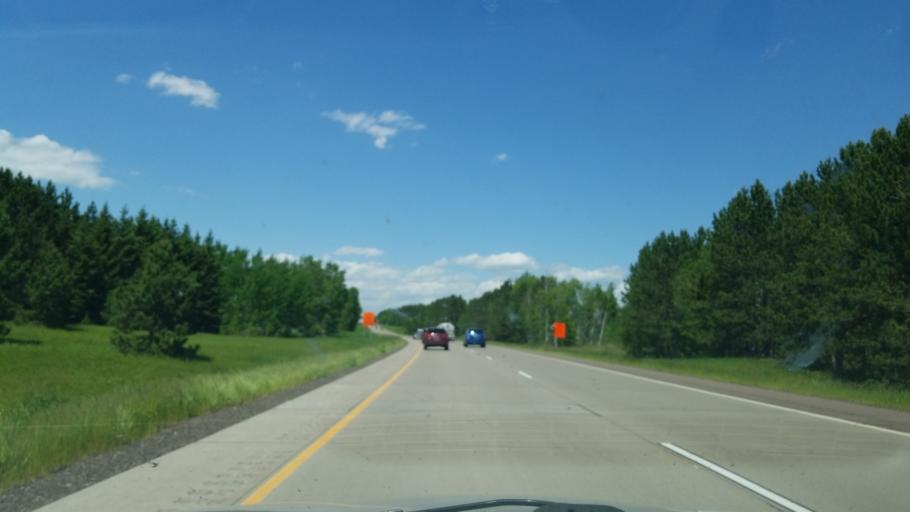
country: US
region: Minnesota
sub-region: Pine County
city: Sandstone
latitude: 46.2337
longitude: -92.8254
